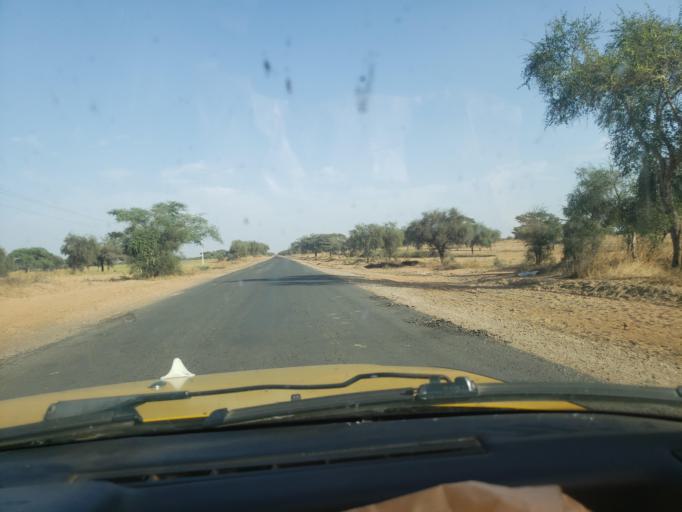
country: SN
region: Louga
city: Louga
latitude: 15.5081
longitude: -15.9726
